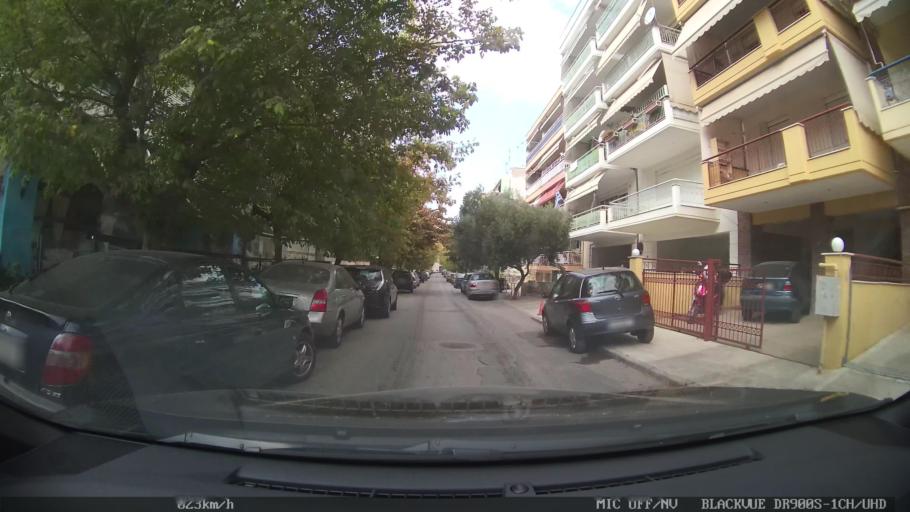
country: GR
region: Central Macedonia
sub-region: Nomos Thessalonikis
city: Triandria
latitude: 40.6136
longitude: 22.9849
